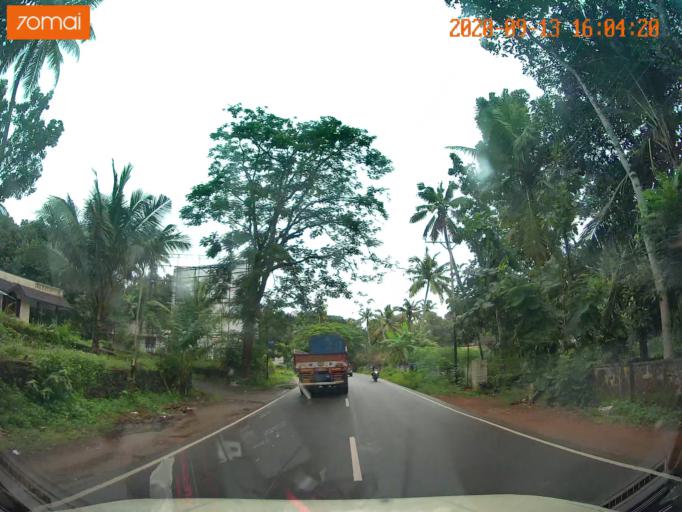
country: IN
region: Kerala
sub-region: Kottayam
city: Palackattumala
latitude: 9.6719
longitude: 76.5697
